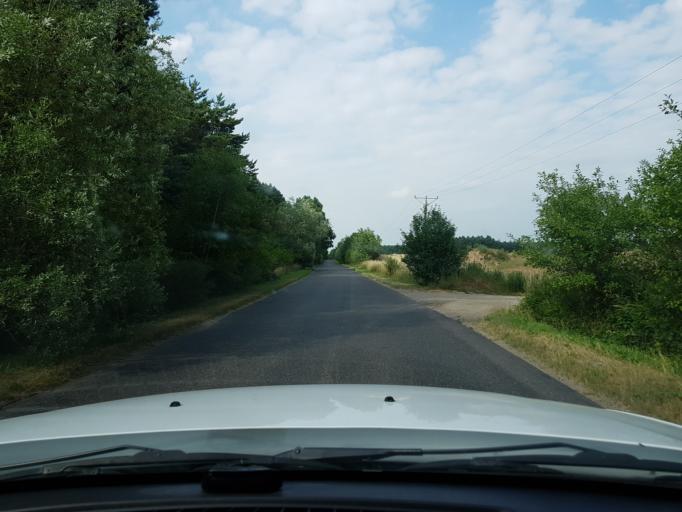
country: PL
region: West Pomeranian Voivodeship
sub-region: Powiat gryfinski
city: Chojna
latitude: 52.9727
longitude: 14.4659
